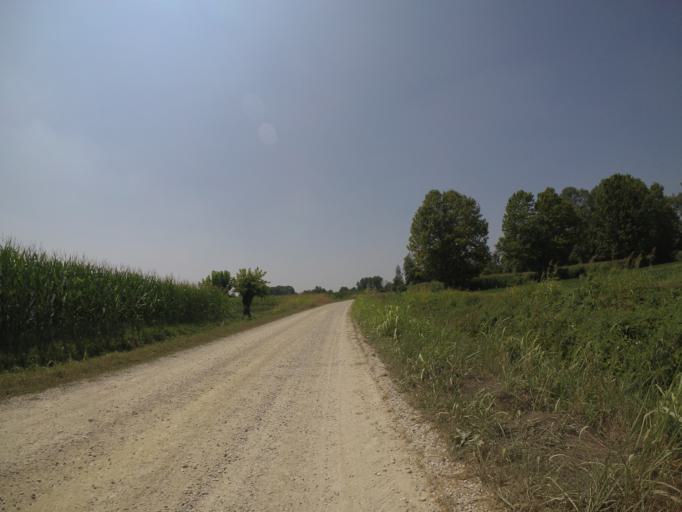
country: IT
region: Friuli Venezia Giulia
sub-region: Provincia di Udine
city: Talmassons
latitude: 45.9144
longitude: 13.1221
